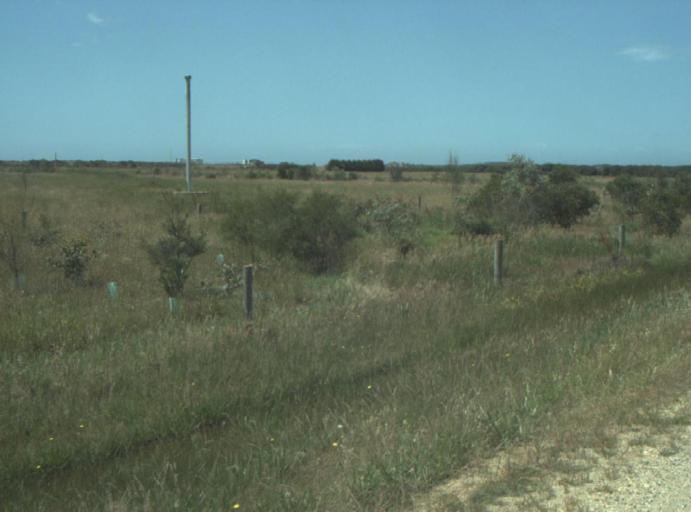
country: AU
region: Victoria
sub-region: Greater Geelong
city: Breakwater
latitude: -38.2698
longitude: 144.4036
